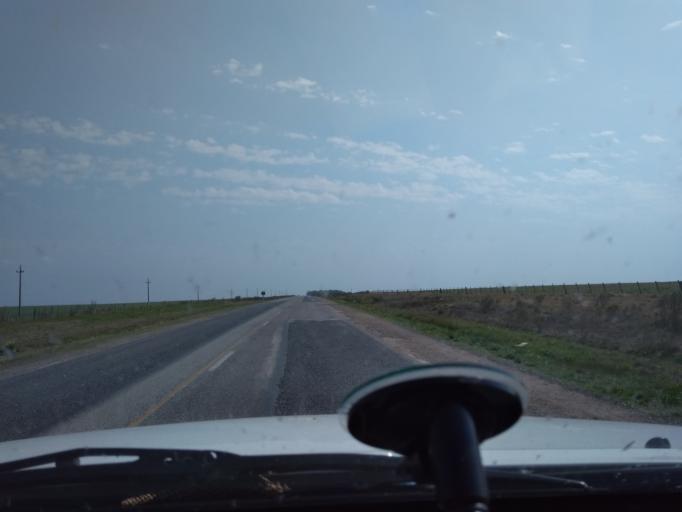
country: UY
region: Florida
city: Florida
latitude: -34.0445
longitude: -55.9884
